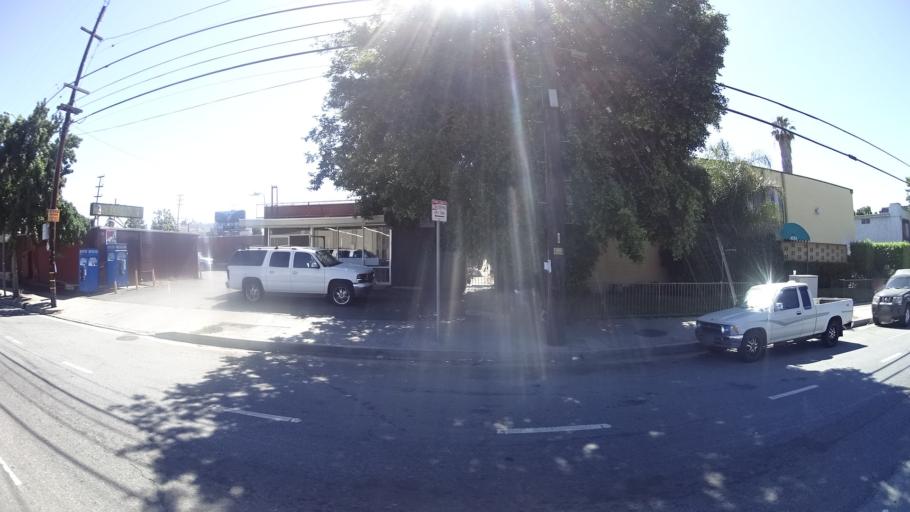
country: US
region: California
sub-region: Los Angeles County
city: Van Nuys
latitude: 34.1932
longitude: -118.4836
